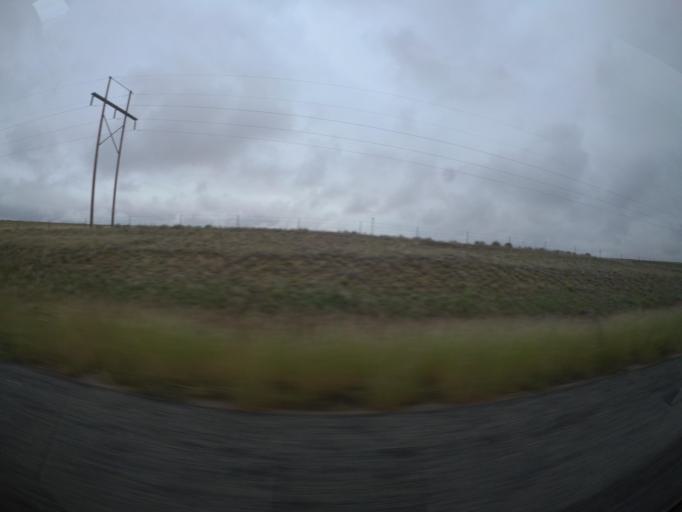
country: US
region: Colorado
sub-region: Washington County
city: Akron
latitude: 39.7395
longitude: -103.4401
